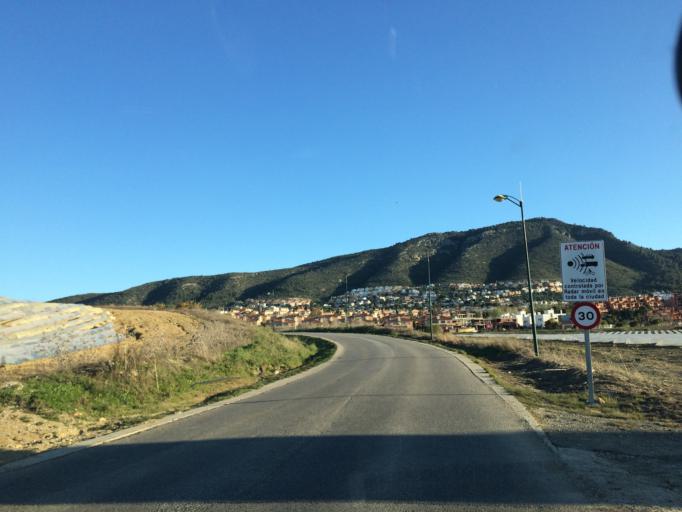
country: ES
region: Andalusia
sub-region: Provincia de Malaga
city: Alhaurin de la Torre
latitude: 36.6698
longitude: -4.5378
